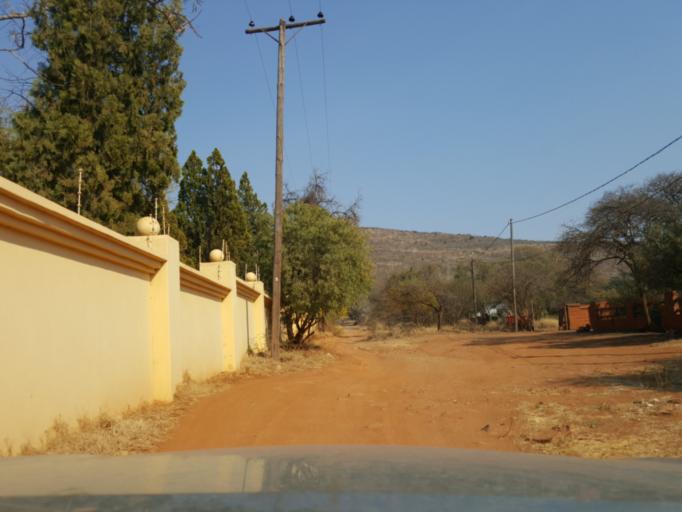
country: BW
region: South East
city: Lobatse
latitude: -25.1772
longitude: 25.6831
